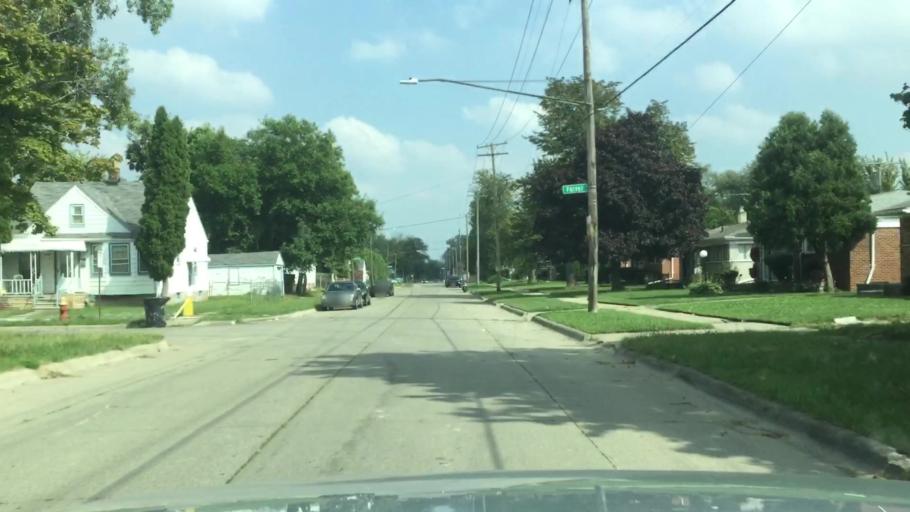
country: US
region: Michigan
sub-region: Wayne County
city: Dearborn
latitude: 42.3605
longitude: -83.2006
